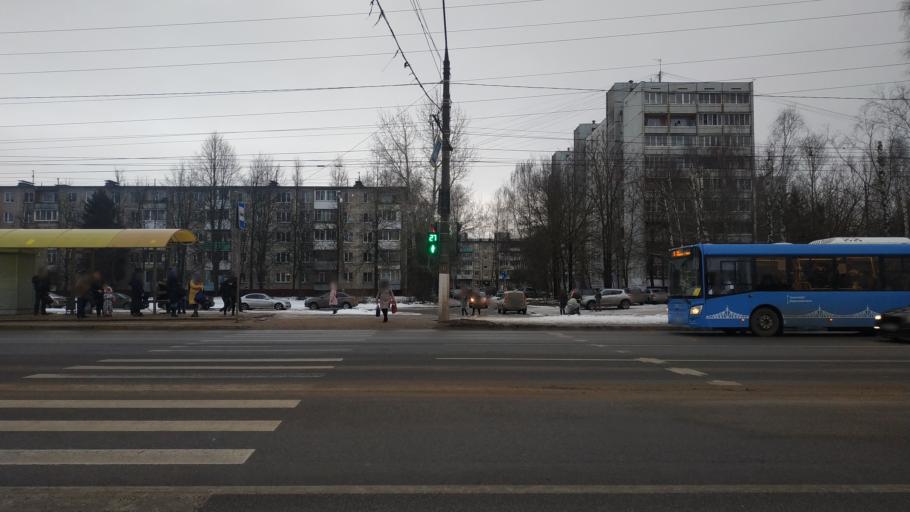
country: RU
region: Tverskaya
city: Tver
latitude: 56.8246
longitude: 35.8926
